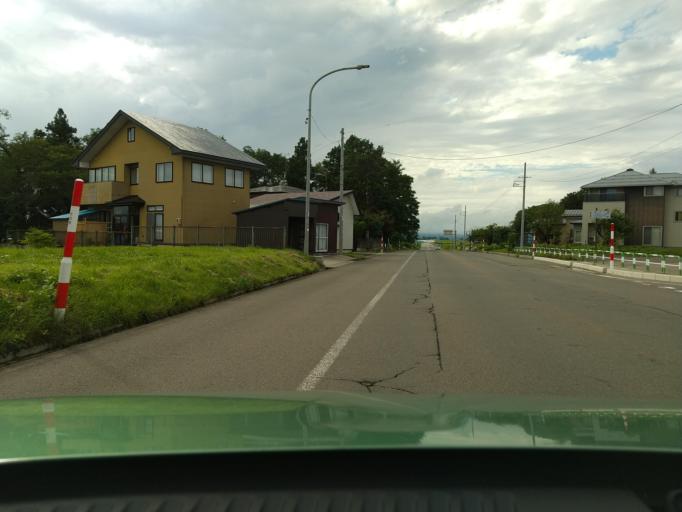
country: JP
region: Akita
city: Yuzawa
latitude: 39.2344
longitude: 140.5104
